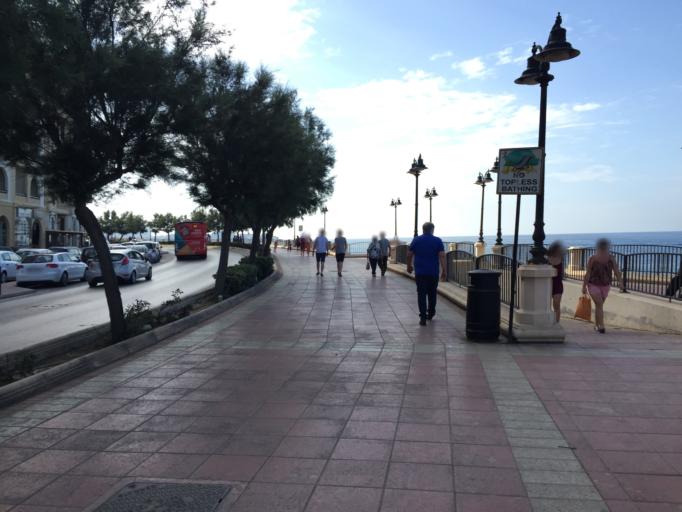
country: MT
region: Tas-Sliema
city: Sliema
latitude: 35.9144
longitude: 14.5068
